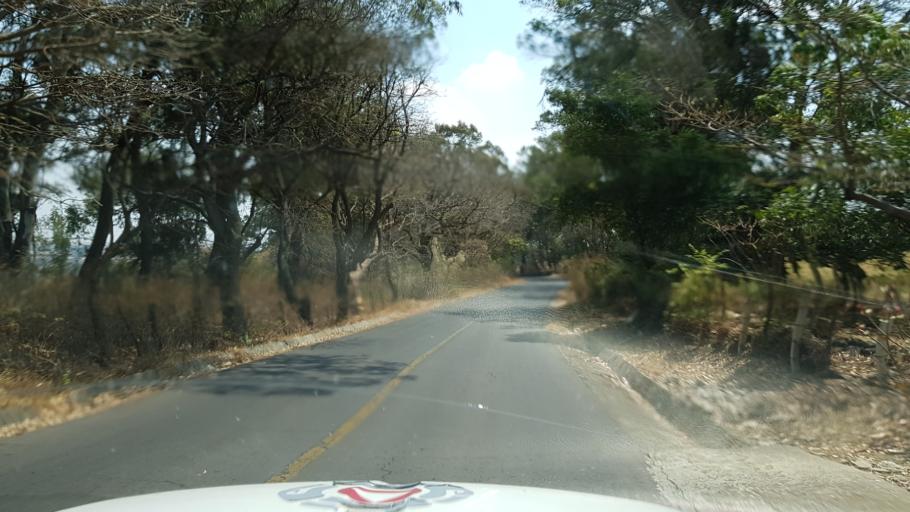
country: MX
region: Morelos
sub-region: Yecapixtla
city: Texcala
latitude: 18.9060
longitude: -98.8083
